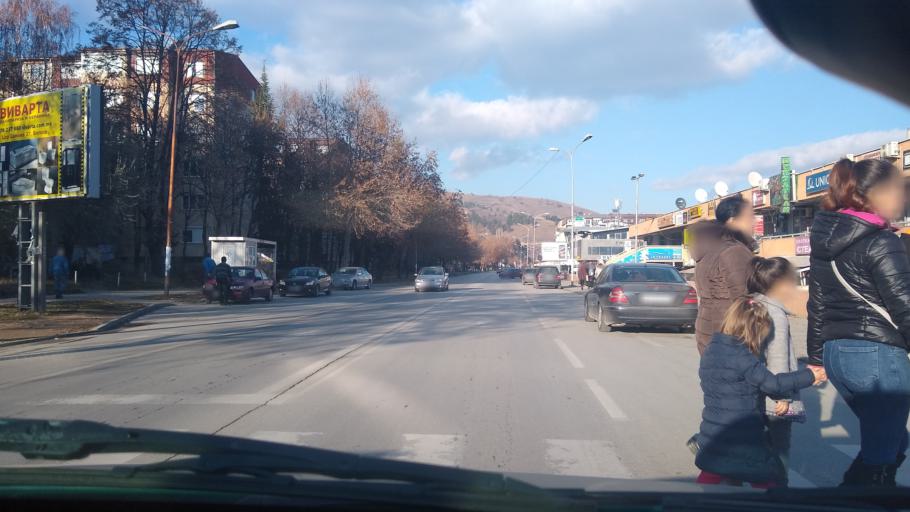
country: MK
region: Bitola
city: Bitola
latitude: 41.0271
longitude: 21.3136
